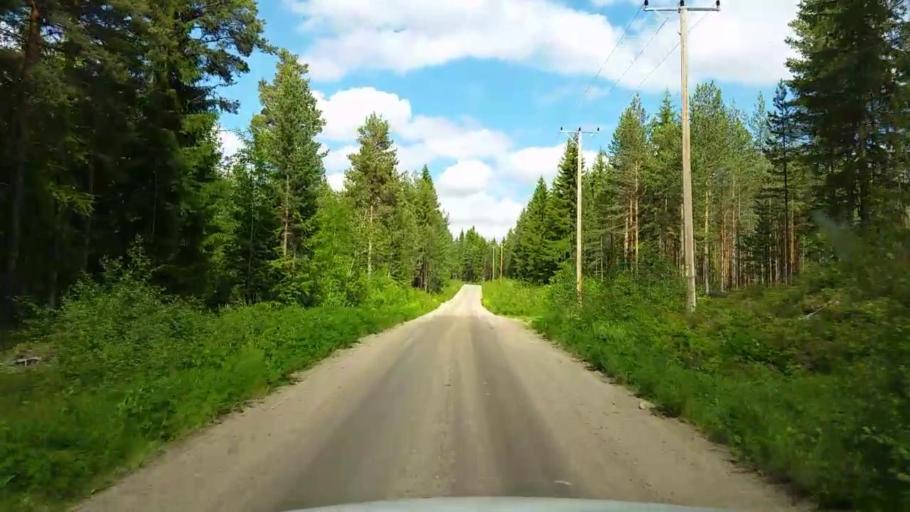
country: SE
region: Gaevleborg
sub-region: Ovanakers Kommun
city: Edsbyn
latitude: 61.5309
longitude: 15.9537
